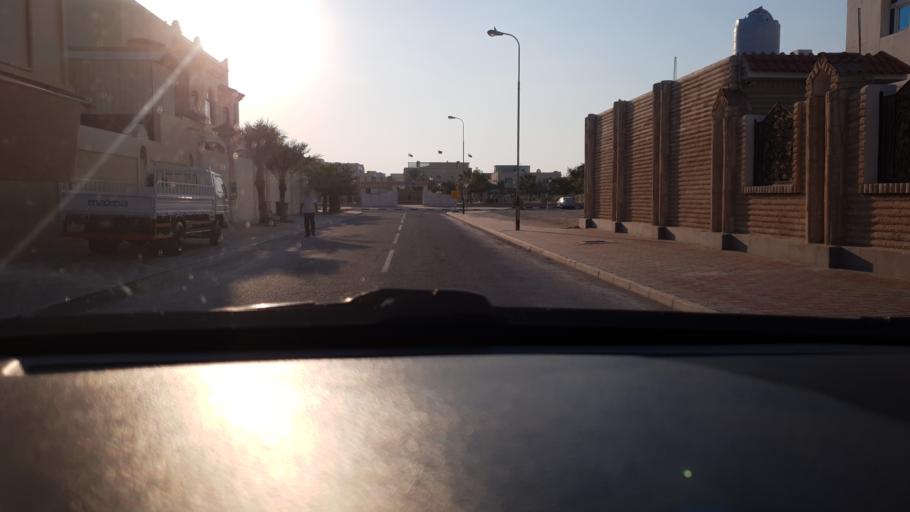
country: QA
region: Baladiyat ad Dawhah
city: Doha
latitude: 25.2353
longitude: 51.5622
